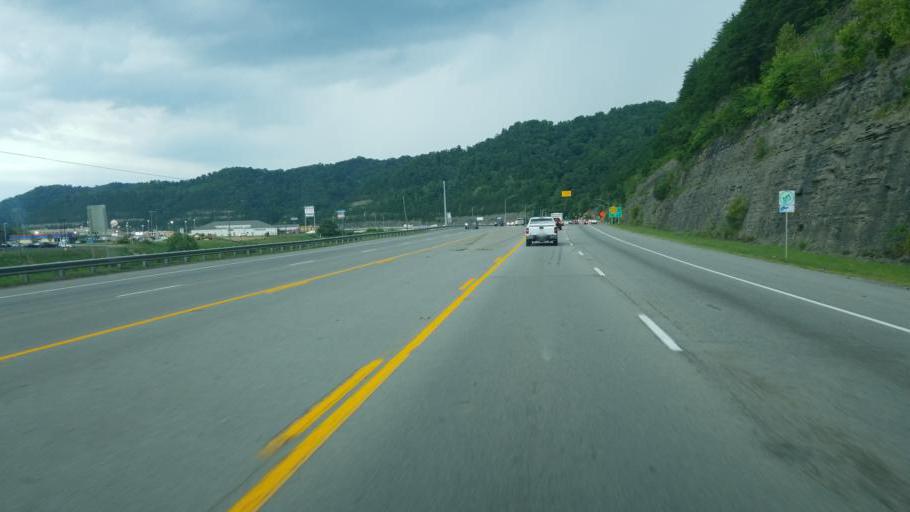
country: US
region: Kentucky
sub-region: Pike County
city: Pikeville
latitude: 37.4997
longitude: -82.5315
